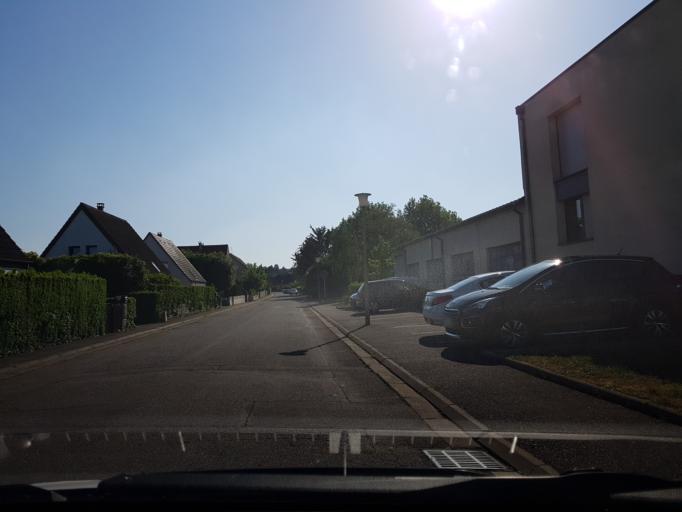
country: FR
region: Alsace
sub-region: Departement du Haut-Rhin
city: Rixheim
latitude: 47.7506
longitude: 7.3963
